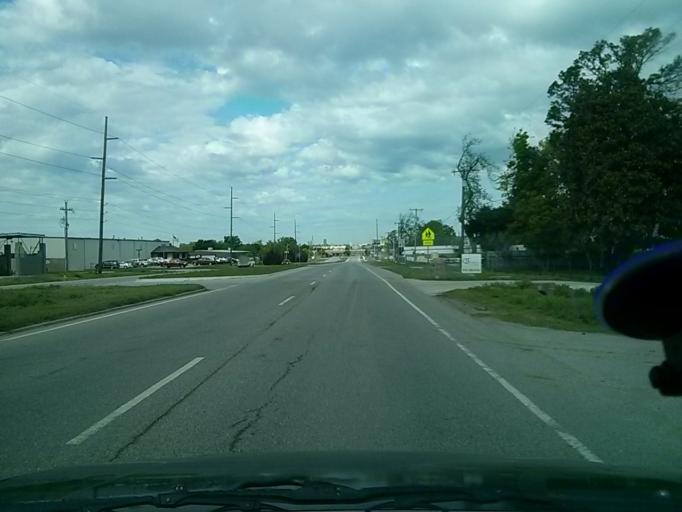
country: US
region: Oklahoma
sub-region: Tulsa County
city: Owasso
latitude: 36.1607
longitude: -95.8521
